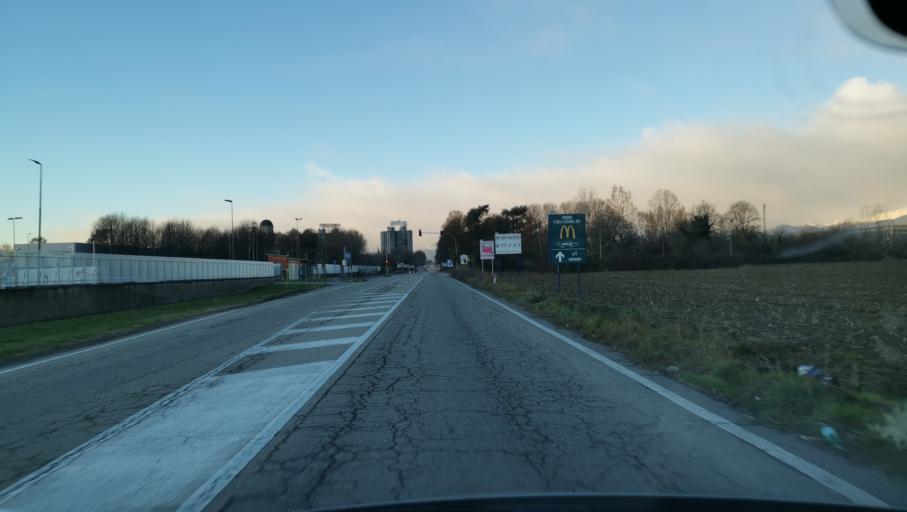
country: IT
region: Piedmont
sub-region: Provincia di Torino
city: Settimo Torinese
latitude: 45.1220
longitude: 7.7209
